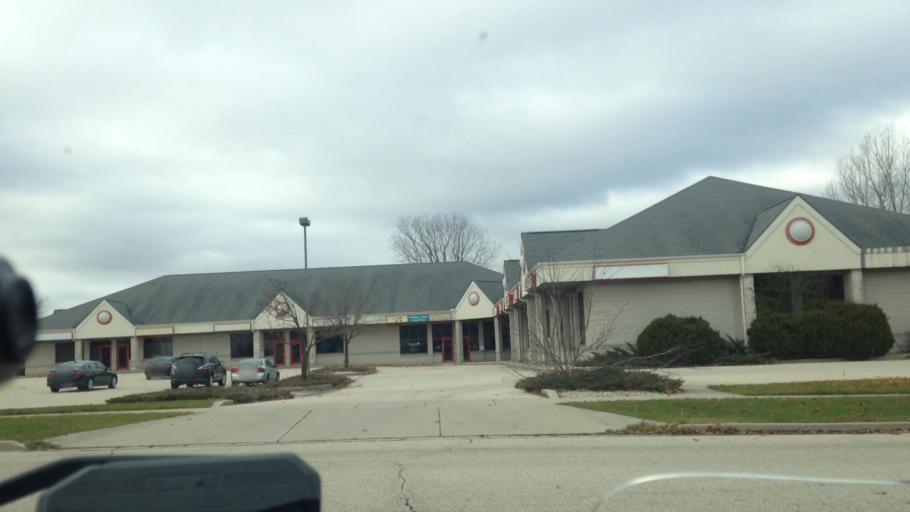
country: US
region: Wisconsin
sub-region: Washington County
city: West Bend
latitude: 43.4288
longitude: -88.2348
